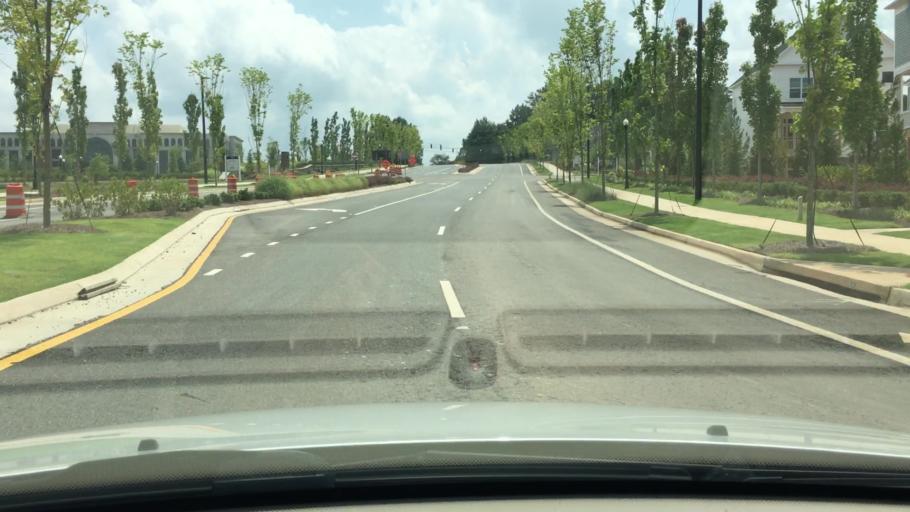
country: US
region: Georgia
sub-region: Fulton County
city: Alpharetta
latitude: 34.0639
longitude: -84.2769
